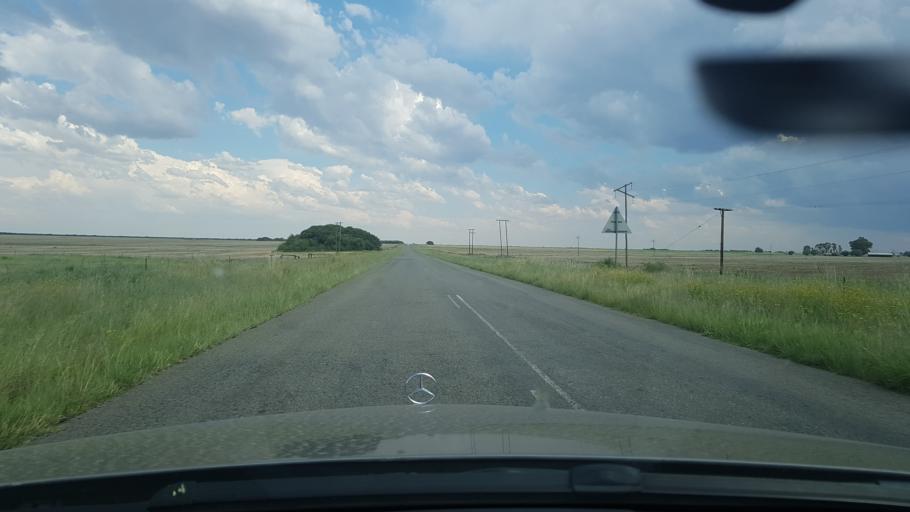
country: ZA
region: North-West
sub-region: Dr Ruth Segomotsi Mompati District Municipality
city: Bloemhof
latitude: -27.8545
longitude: 25.6495
